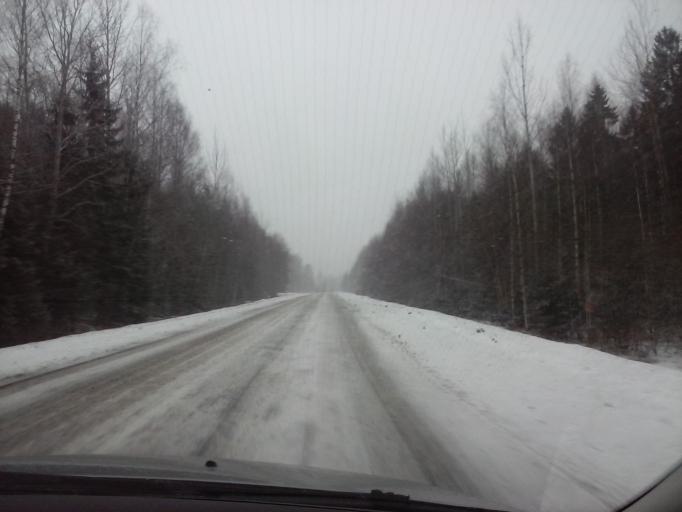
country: LV
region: Valkas Rajons
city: Valka
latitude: 57.7213
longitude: 25.9345
